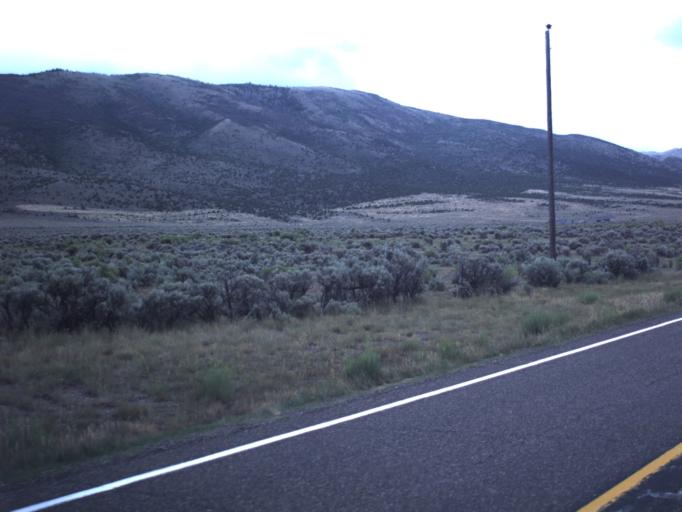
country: US
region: Utah
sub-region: Wayne County
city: Loa
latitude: 38.5767
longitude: -111.8425
